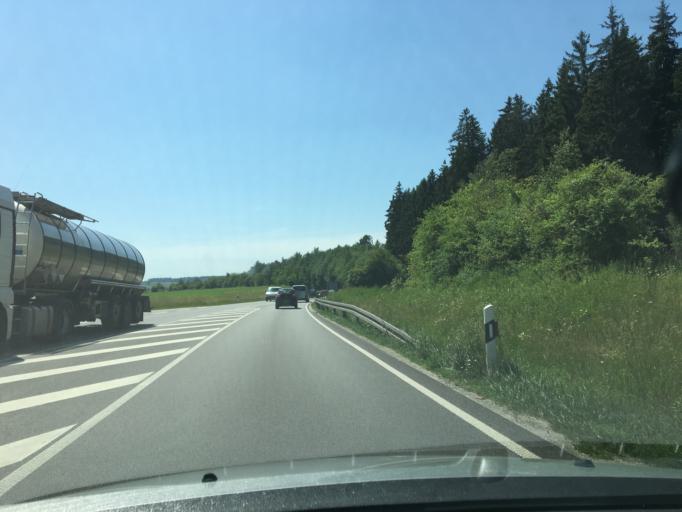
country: DE
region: Bavaria
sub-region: Lower Bavaria
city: Vilsbiburg
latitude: 48.4469
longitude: 12.3378
